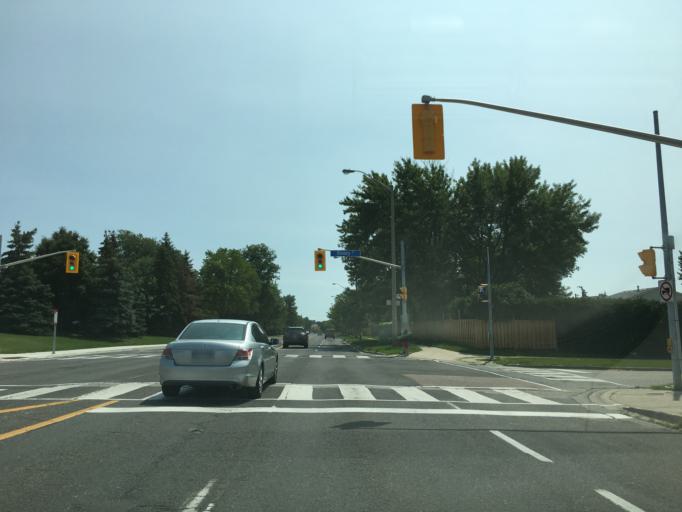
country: CA
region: Ontario
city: Scarborough
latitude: 43.8073
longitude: -79.3106
